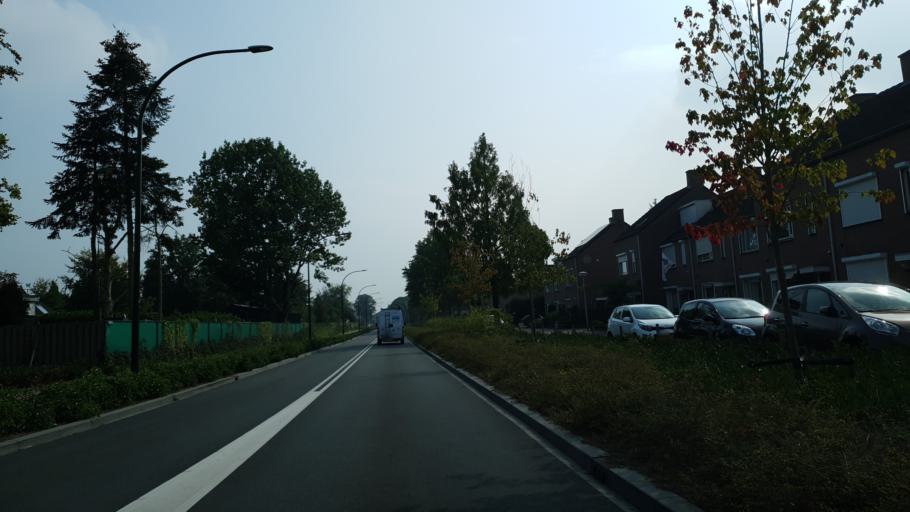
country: NL
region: North Brabant
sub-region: Gemeente Valkenswaard
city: Valkenswaard
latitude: 51.3508
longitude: 5.4651
